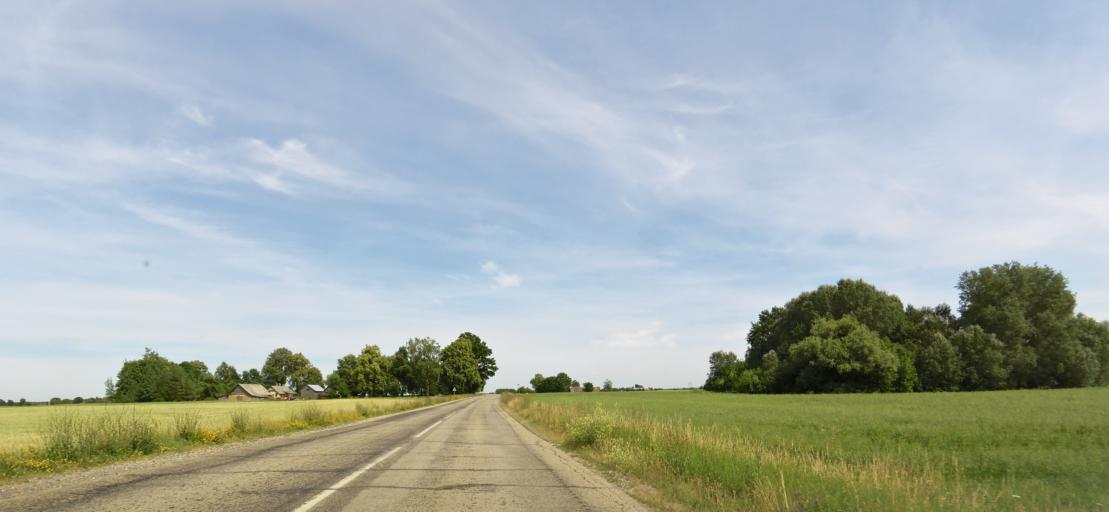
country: LT
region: Panevezys
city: Pasvalys
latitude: 55.9326
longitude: 24.2940
